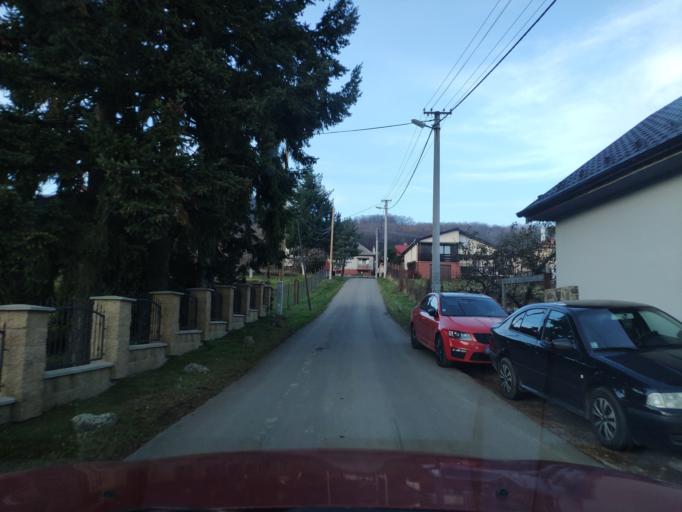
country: SK
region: Kosicky
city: Secovce
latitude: 48.6342
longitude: 21.4674
